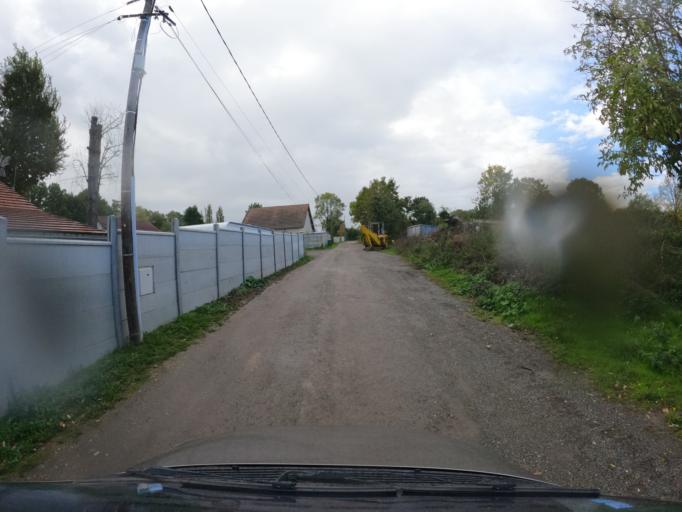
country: FR
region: Ile-de-France
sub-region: Departement de Seine-et-Marne
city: Saint-Germain-sur-Morin
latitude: 48.8729
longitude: 2.8536
